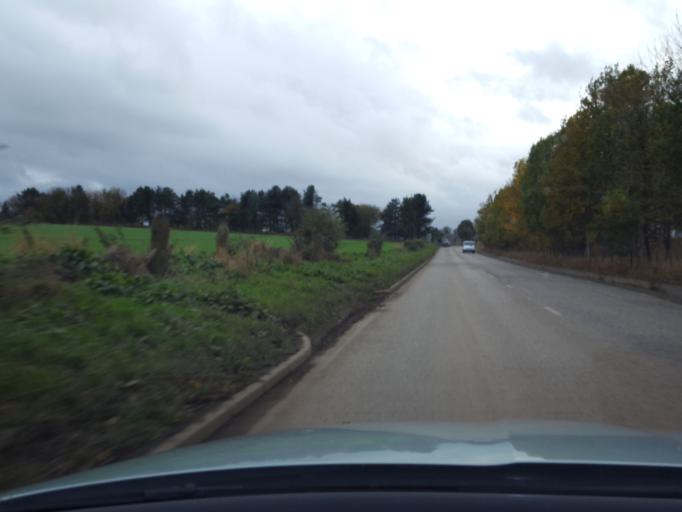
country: GB
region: Scotland
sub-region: Edinburgh
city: Newbridge
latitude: 55.9127
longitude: -3.4018
